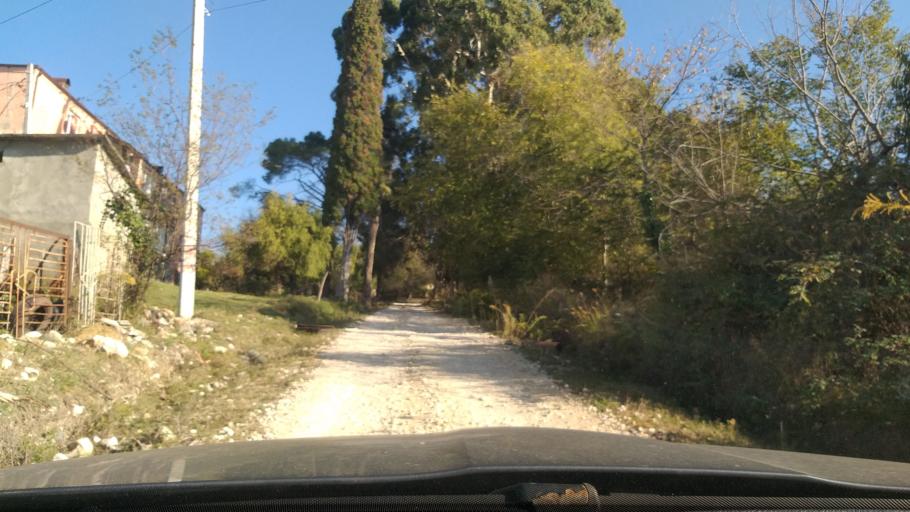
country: GE
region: Abkhazia
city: Stantsiya Novyy Afon
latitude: 43.0486
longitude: 40.8991
